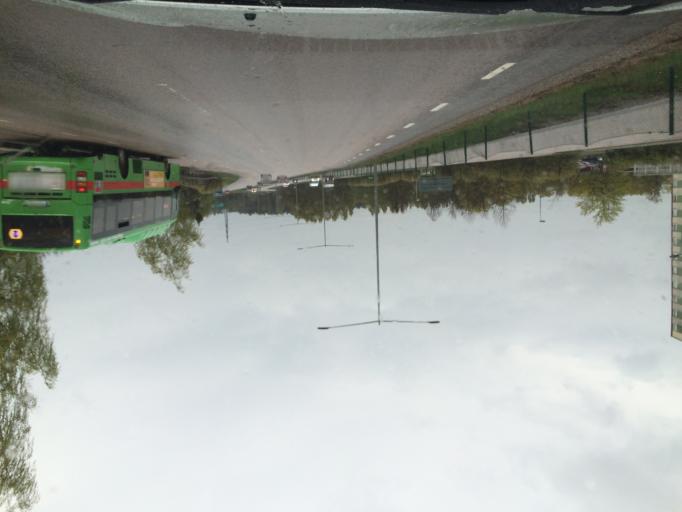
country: SE
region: Soedermanland
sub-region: Eskilstuna Kommun
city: Eskilstuna
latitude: 59.3817
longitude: 16.5237
